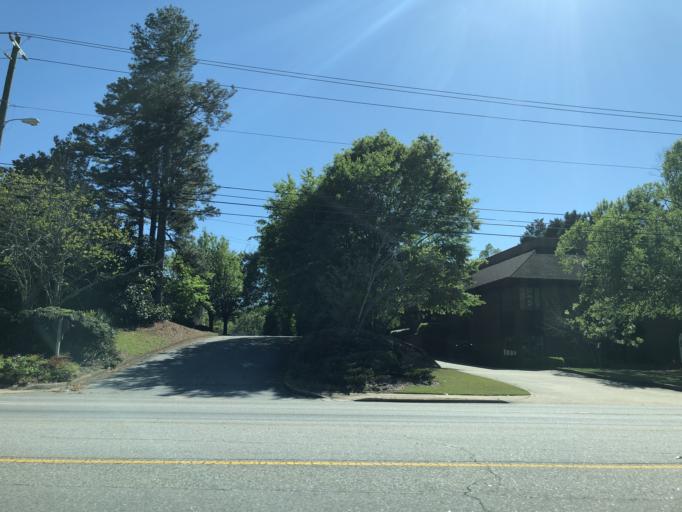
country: US
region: Georgia
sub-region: Clarke County
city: Country Club Estates
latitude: 33.9703
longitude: -83.4101
